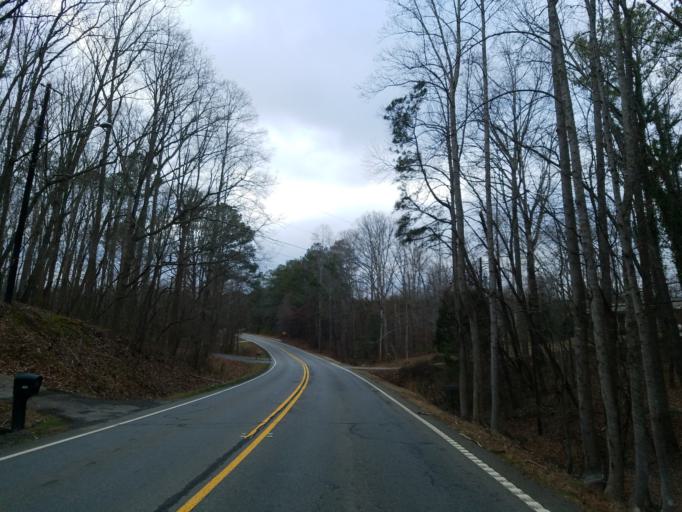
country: US
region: Georgia
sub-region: Cherokee County
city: Canton
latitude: 34.3127
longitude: -84.5406
